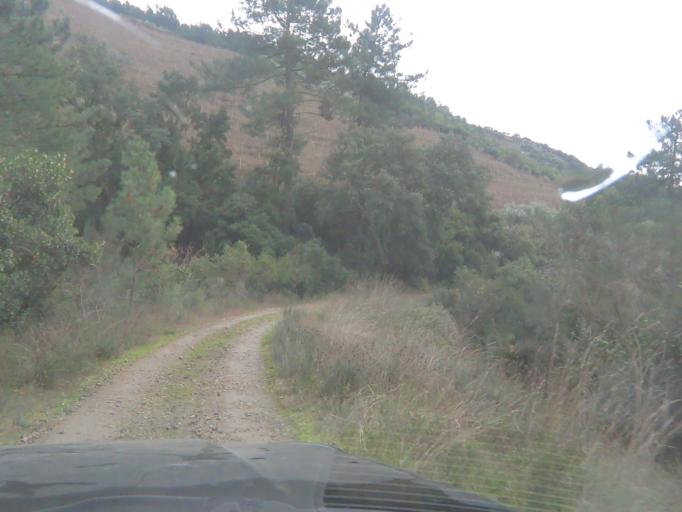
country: PT
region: Vila Real
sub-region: Vila Real
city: Vila Real
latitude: 41.2556
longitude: -7.7446
